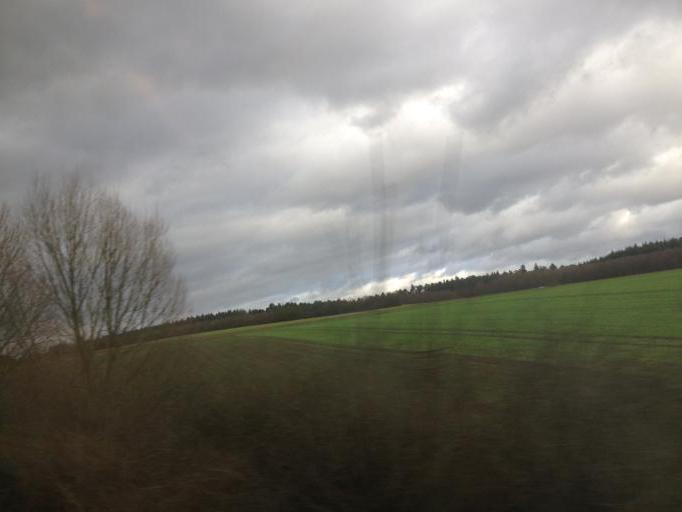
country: DE
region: Hesse
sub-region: Regierungsbezirk Giessen
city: Lich
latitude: 50.5195
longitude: 8.7654
